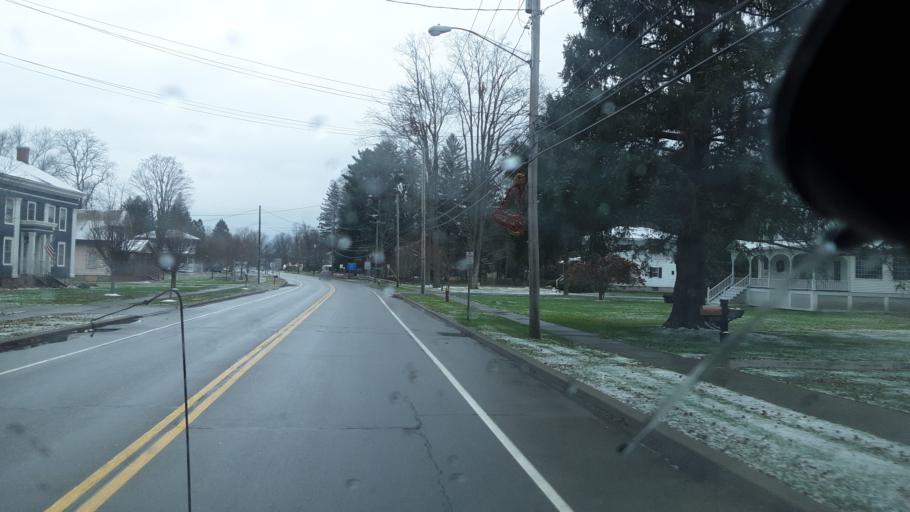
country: US
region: New York
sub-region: Cattaraugus County
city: Portville
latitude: 42.0423
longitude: -78.3446
